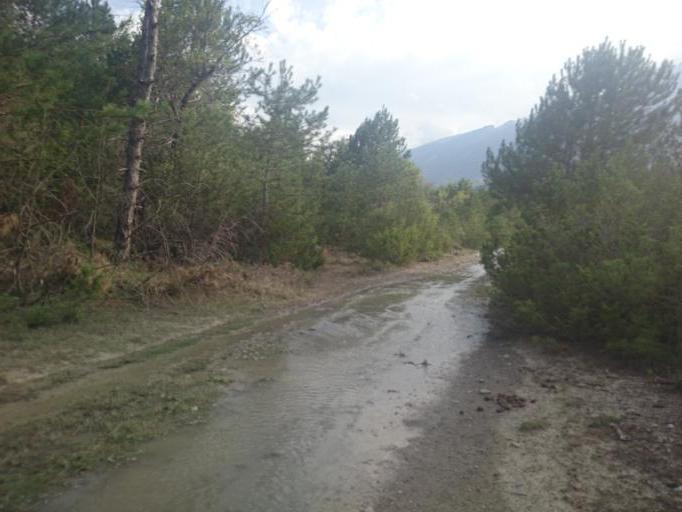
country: AL
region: Elbasan
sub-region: Rrethi i Gramshit
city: Skenderbegas
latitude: 40.7558
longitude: 20.2117
